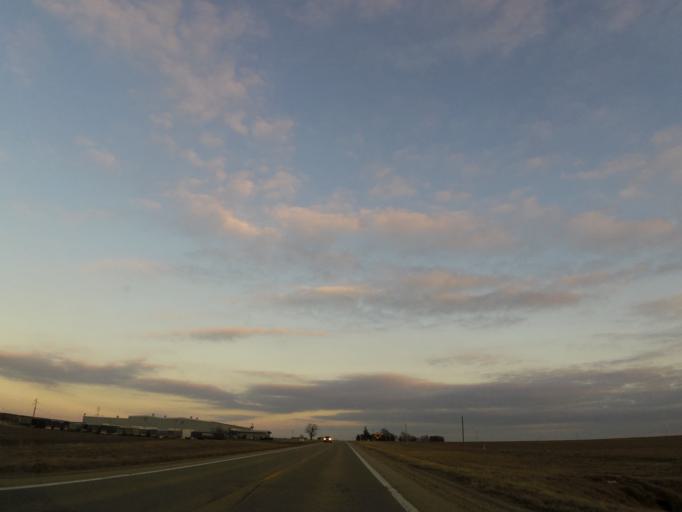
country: US
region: Illinois
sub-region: McLean County
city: Gridley
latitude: 40.7389
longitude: -88.9342
